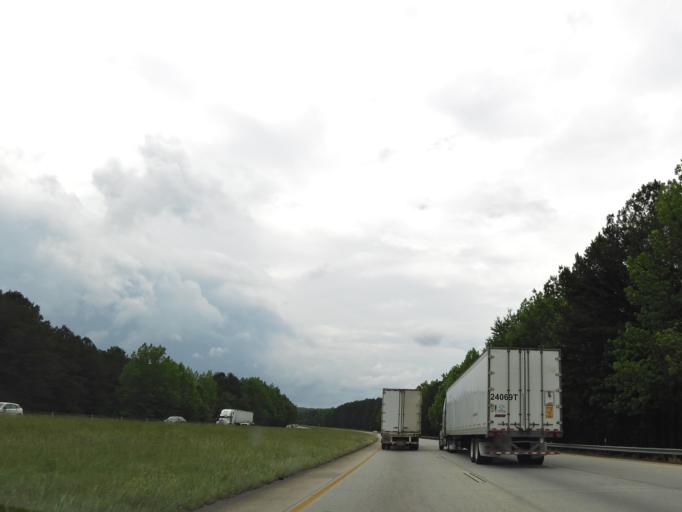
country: US
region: Georgia
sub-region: Carroll County
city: Temple
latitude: 33.7160
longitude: -85.0338
